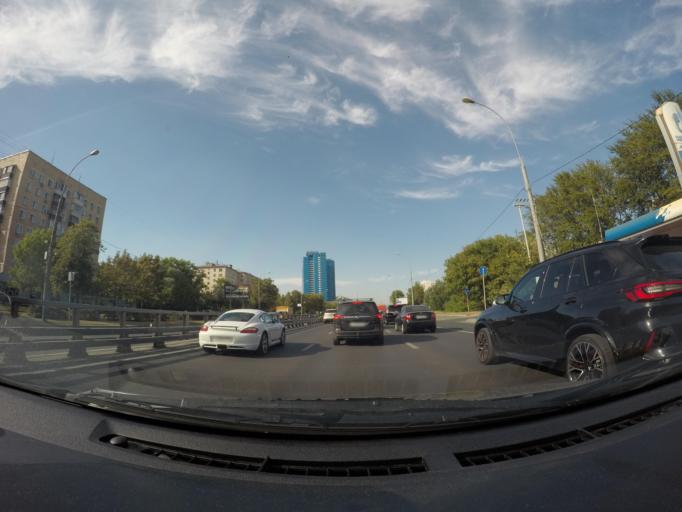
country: RU
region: Moscow
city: Likhobory
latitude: 55.8228
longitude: 37.5731
